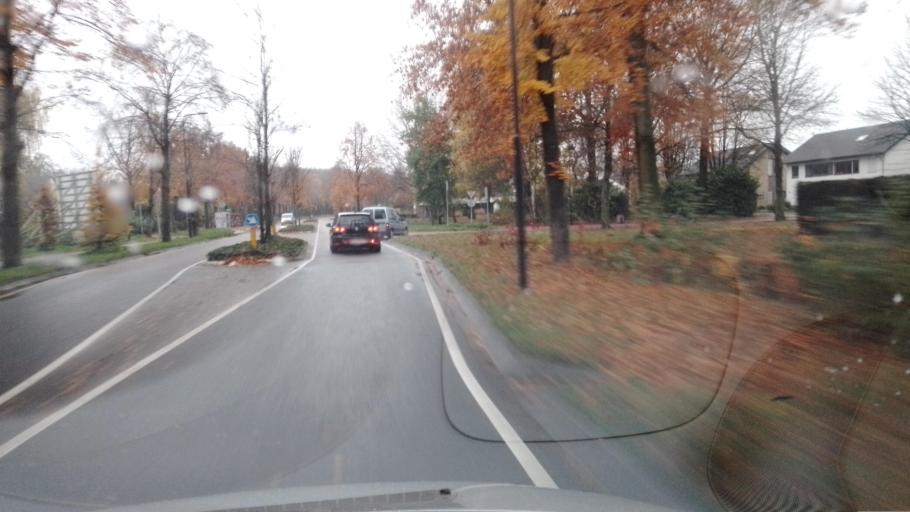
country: NL
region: North Brabant
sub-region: Gemeente Asten
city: Asten
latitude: 51.4097
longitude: 5.7565
